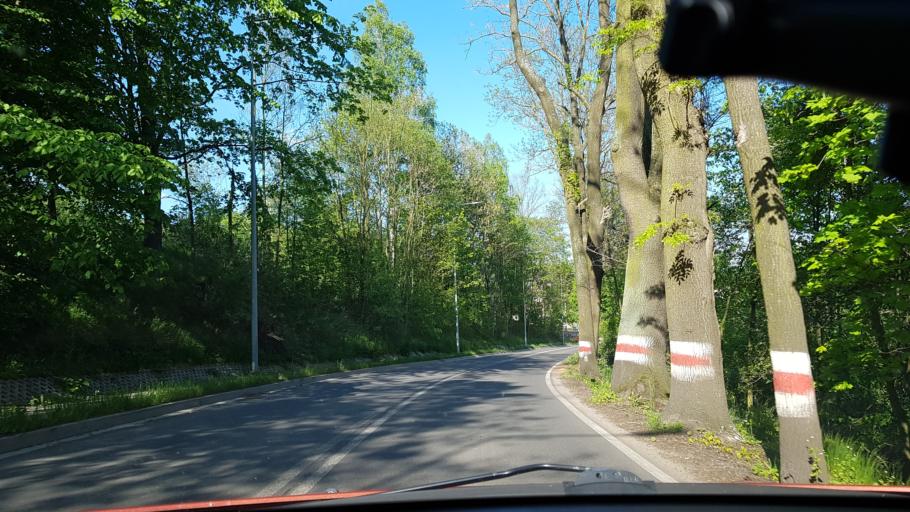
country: PL
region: Lower Silesian Voivodeship
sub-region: Powiat klodzki
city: Nowa Ruda
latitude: 50.5798
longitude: 16.4848
